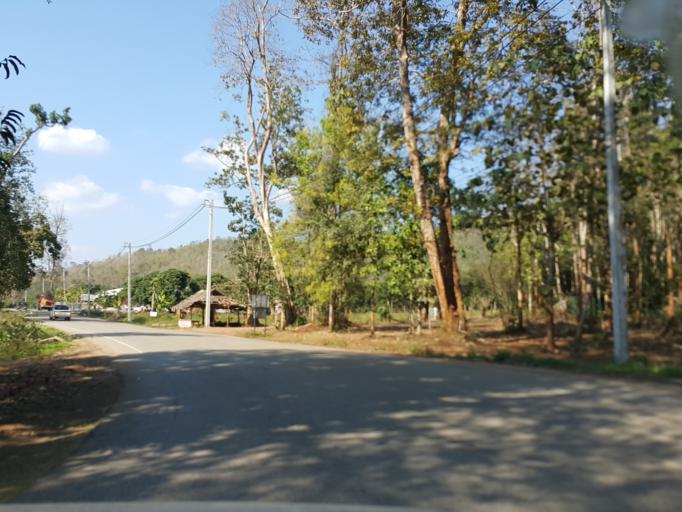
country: TH
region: Chiang Mai
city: Mae Wang
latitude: 18.6415
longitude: 98.7000
